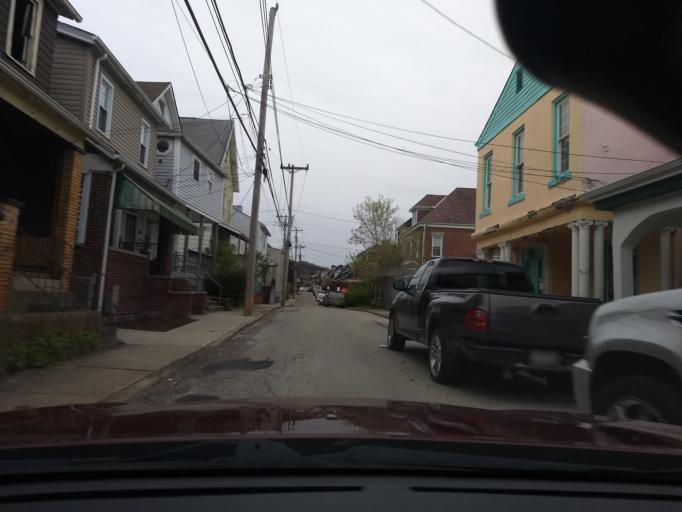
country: US
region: Pennsylvania
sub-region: Allegheny County
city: McKees Rocks
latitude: 40.4641
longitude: -80.0694
